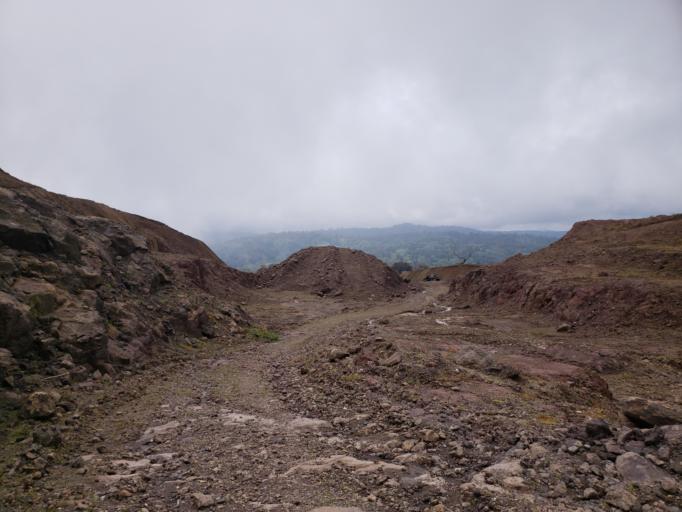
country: ET
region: Oromiya
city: Dodola
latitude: 6.6554
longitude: 39.3627
